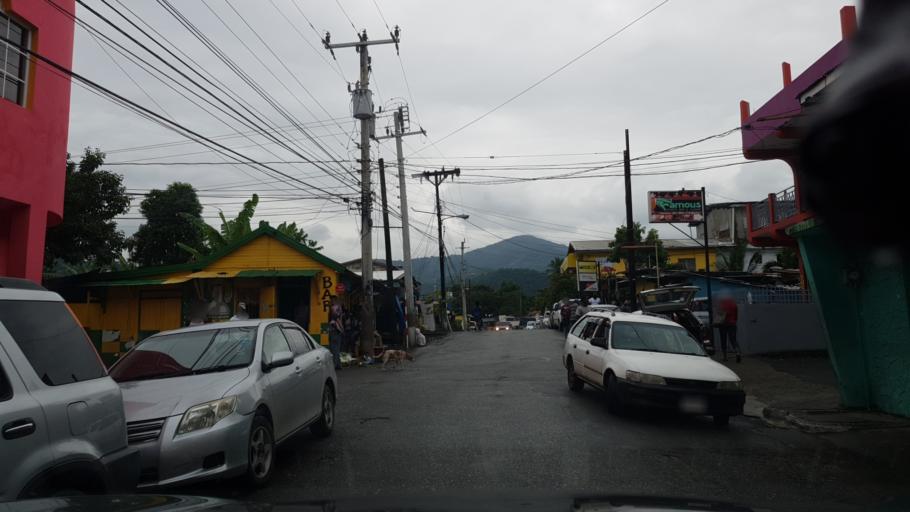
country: JM
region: Portland
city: Buff Bay
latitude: 18.2336
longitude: -76.6604
